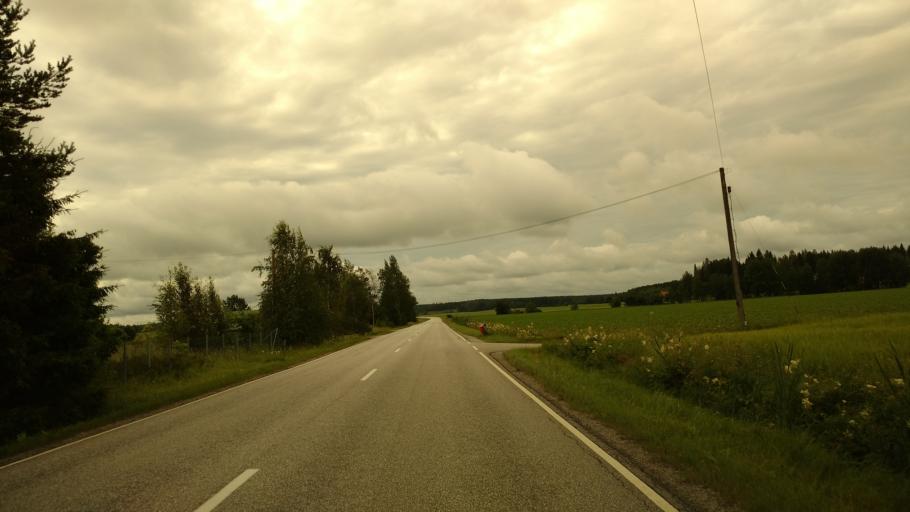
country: FI
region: Varsinais-Suomi
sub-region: Salo
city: Kuusjoki
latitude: 60.4780
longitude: 23.1596
